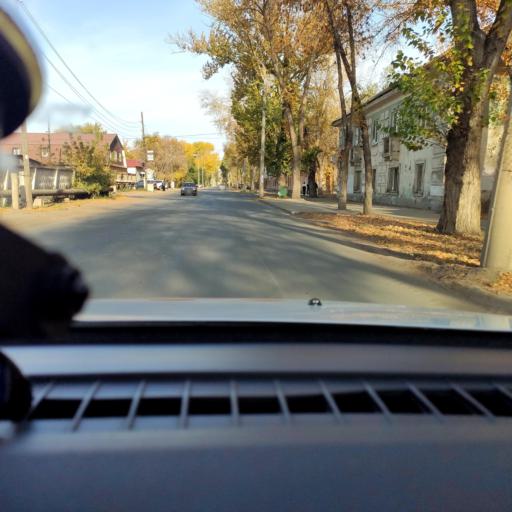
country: RU
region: Samara
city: Samara
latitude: 53.1112
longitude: 50.0757
